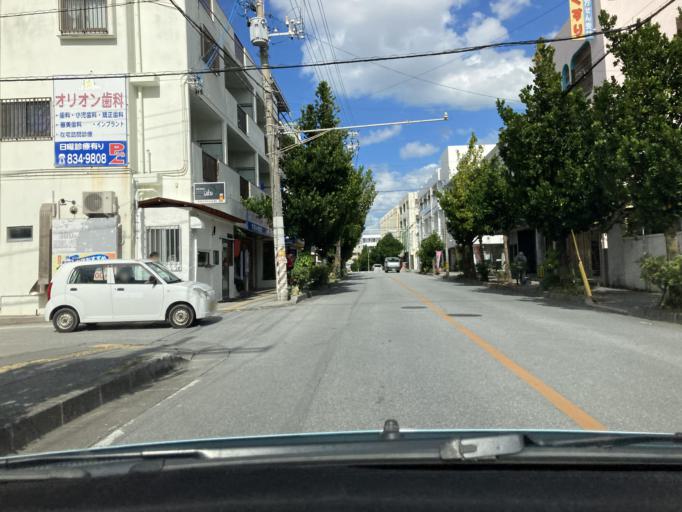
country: JP
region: Okinawa
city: Naha-shi
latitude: 26.2117
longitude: 127.6995
